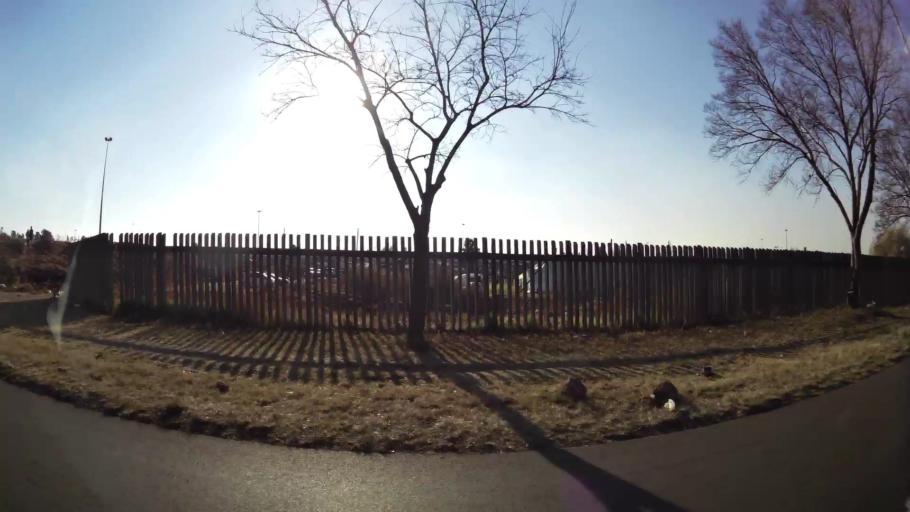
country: ZA
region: Gauteng
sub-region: City of Johannesburg Metropolitan Municipality
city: Soweto
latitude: -26.2664
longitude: 27.8674
